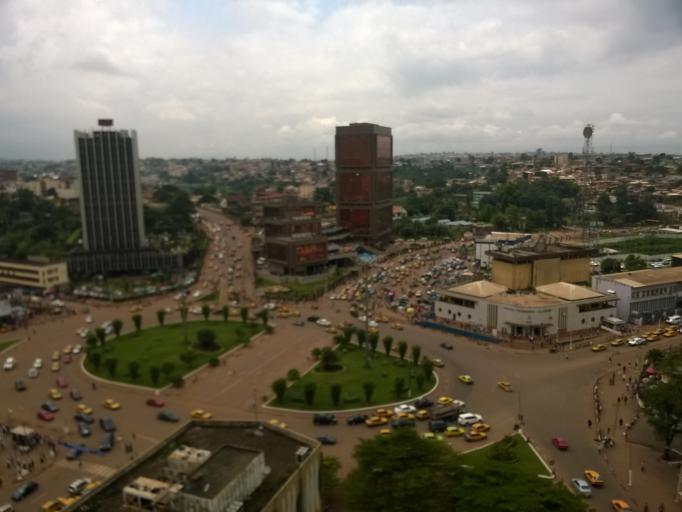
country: CM
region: Centre
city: Yaounde
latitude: 3.8617
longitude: 11.5193
